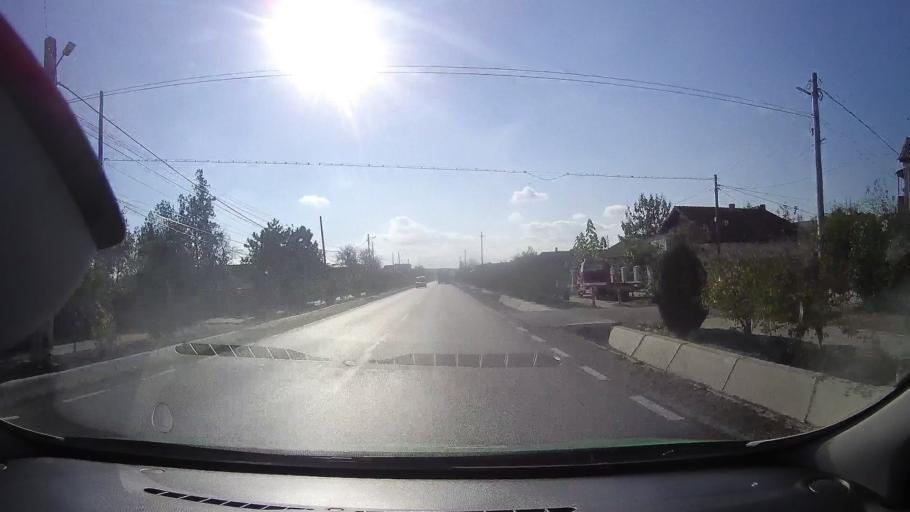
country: RO
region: Tulcea
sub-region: Comuna Baia
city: Baia
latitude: 44.7295
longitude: 28.6812
